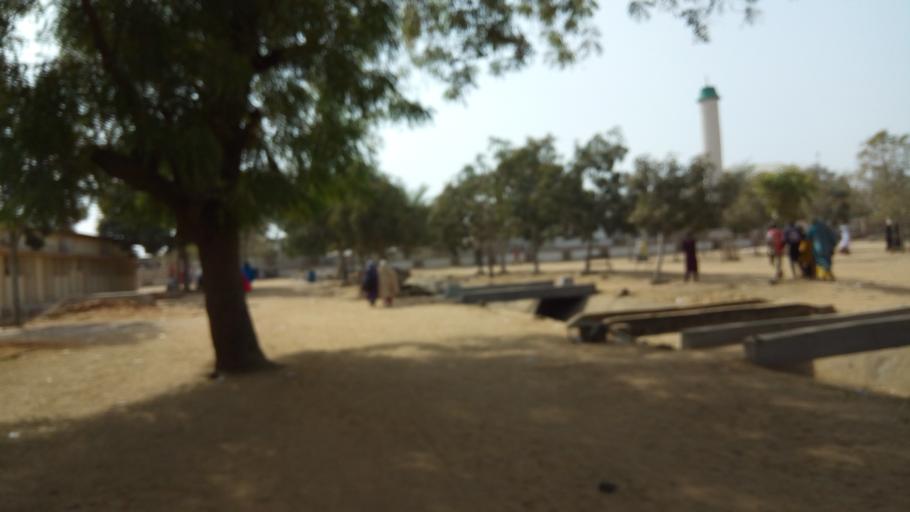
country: NG
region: Gombe
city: Gombe
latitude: 10.3069
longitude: 11.1725
